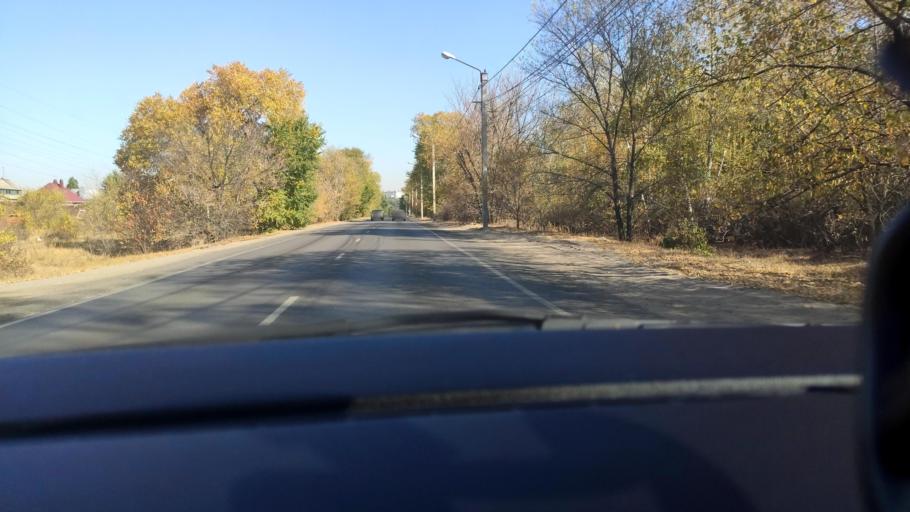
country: RU
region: Voronezj
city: Pridonskoy
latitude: 51.6396
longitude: 39.0899
